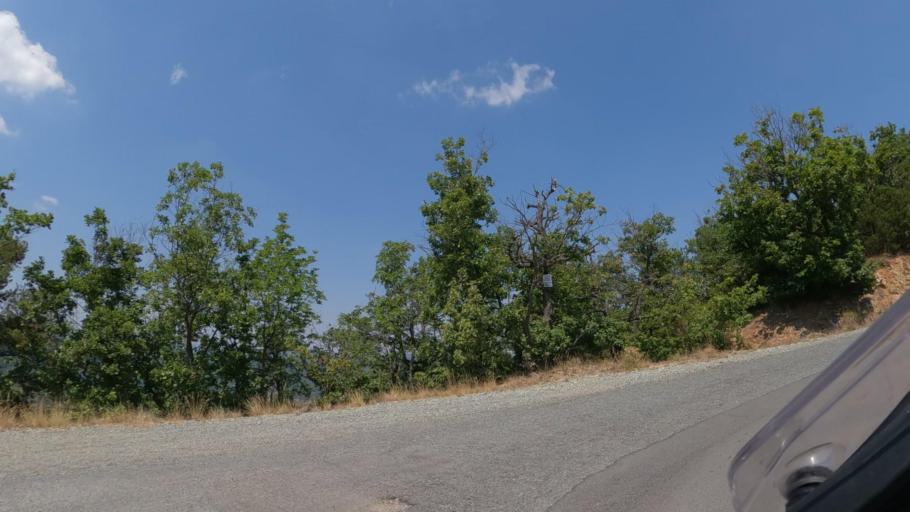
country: IT
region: Piedmont
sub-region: Provincia di Alessandria
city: Ponzone
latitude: 44.5418
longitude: 8.4712
